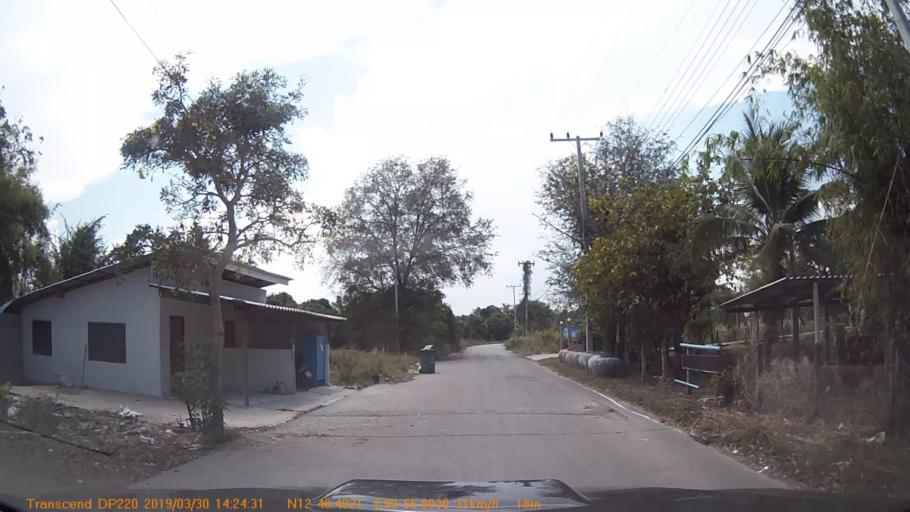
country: TH
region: Prachuap Khiri Khan
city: Hua Hin
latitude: 12.6747
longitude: 99.9299
